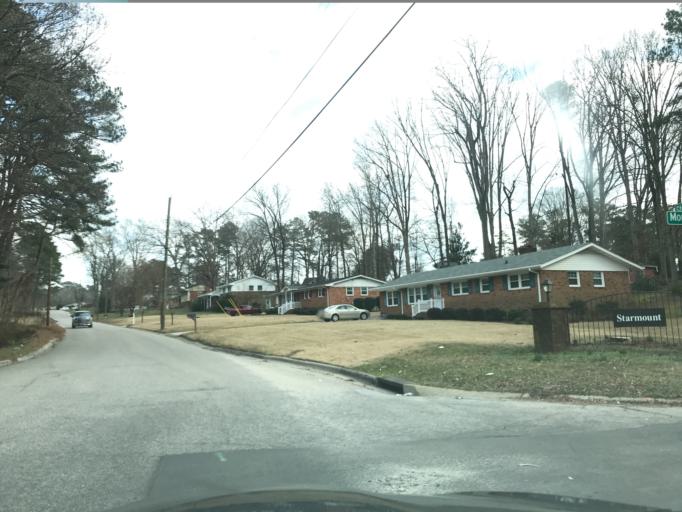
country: US
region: North Carolina
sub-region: Wake County
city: Raleigh
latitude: 35.8233
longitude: -78.5855
